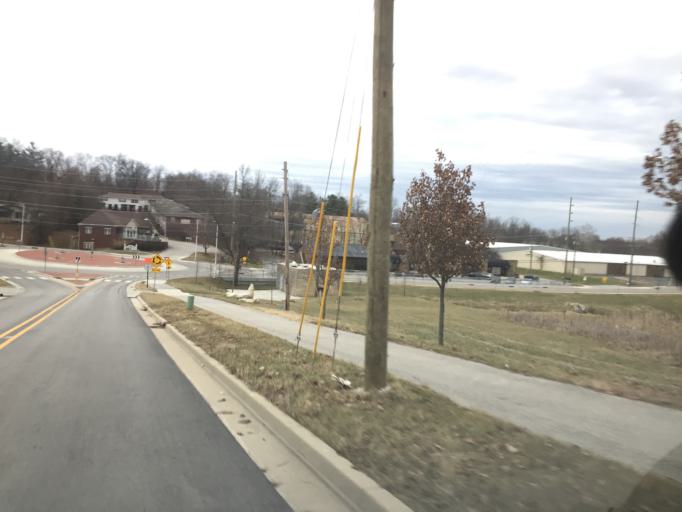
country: US
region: Indiana
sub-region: Monroe County
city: Bloomington
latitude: 39.1781
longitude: -86.5471
